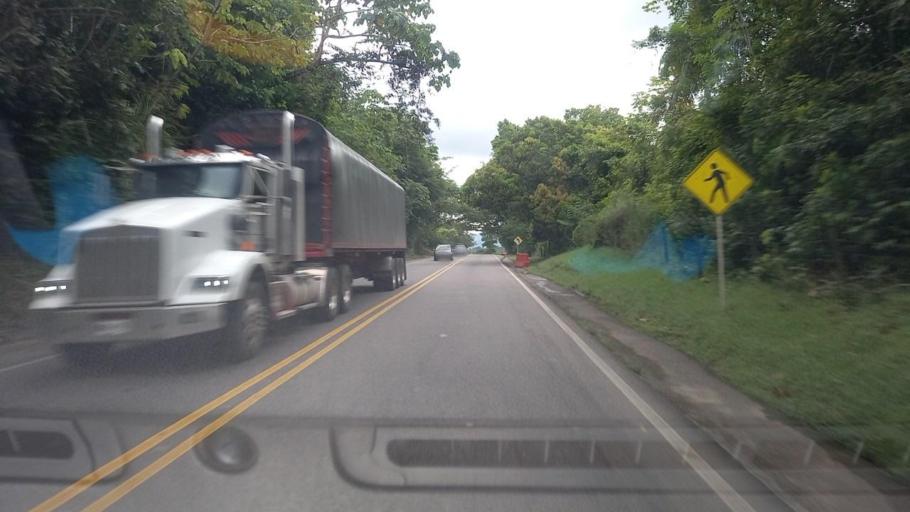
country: CO
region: Santander
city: Barrancabermeja
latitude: 7.1199
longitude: -73.6035
